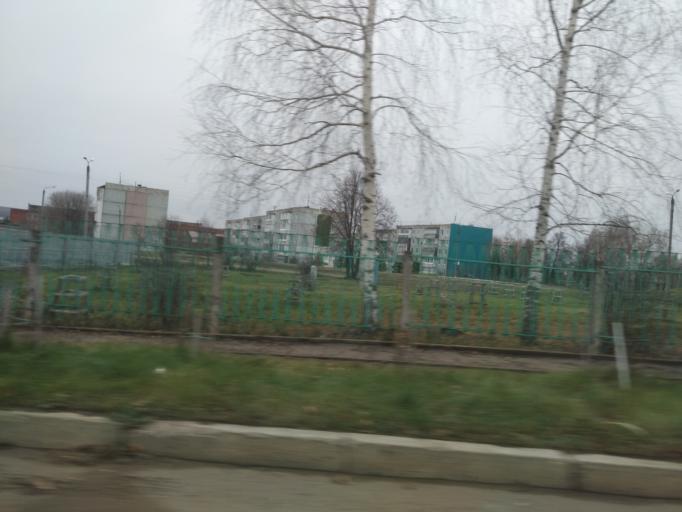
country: RU
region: Kirov
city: Vyatskiye Polyany
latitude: 56.2289
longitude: 51.0739
